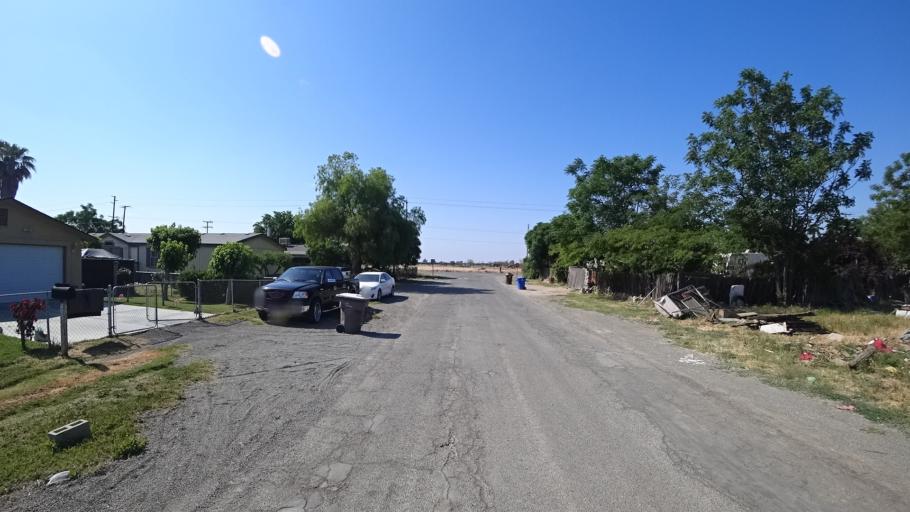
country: US
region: California
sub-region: Kings County
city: Home Garden
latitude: 36.2993
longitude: -119.6354
